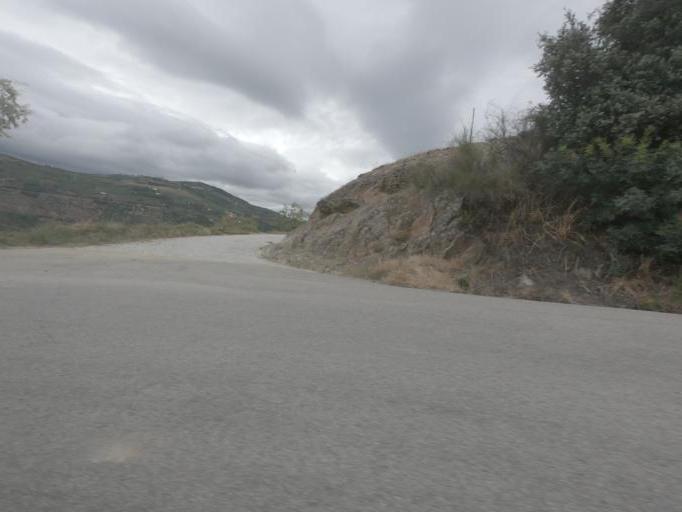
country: PT
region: Vila Real
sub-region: Sabrosa
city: Vilela
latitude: 41.2082
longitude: -7.5346
